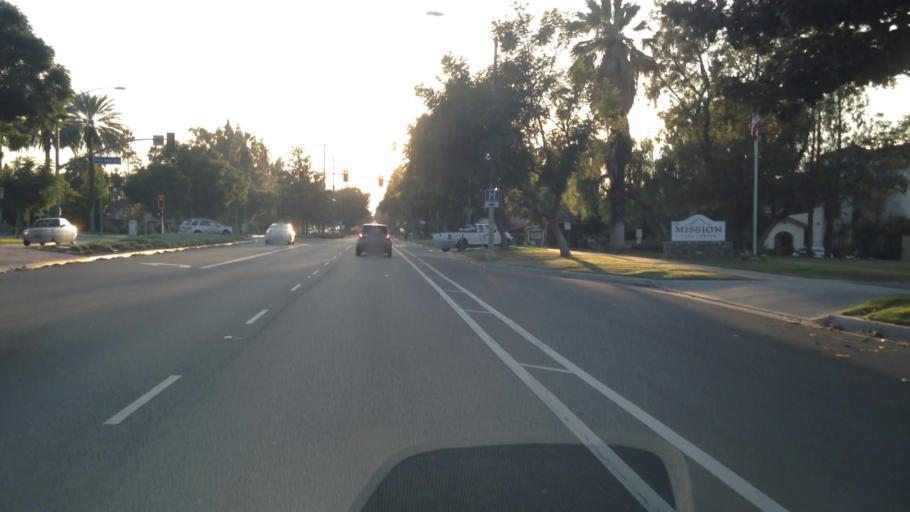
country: US
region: California
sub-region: Riverside County
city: Riverside
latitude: 33.9313
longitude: -117.4275
